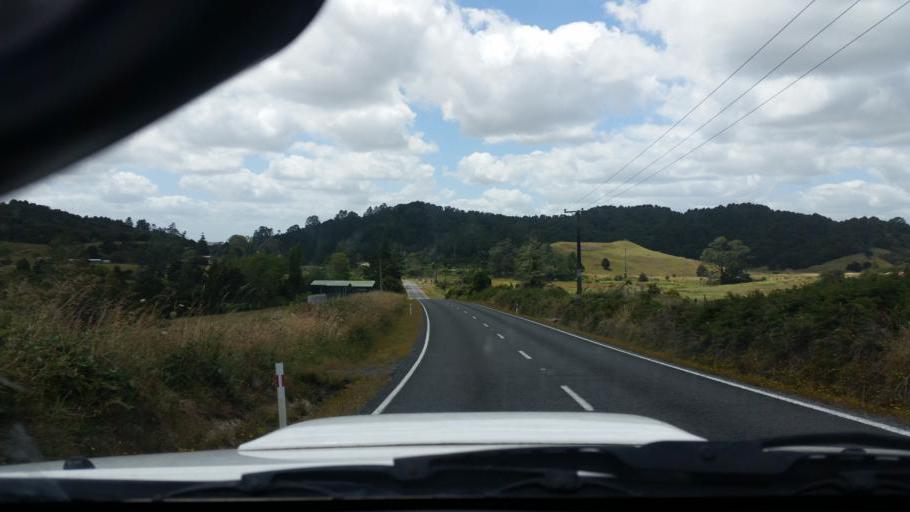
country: NZ
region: Northland
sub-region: Whangarei
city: Ruakaka
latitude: -36.0437
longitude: 174.2788
